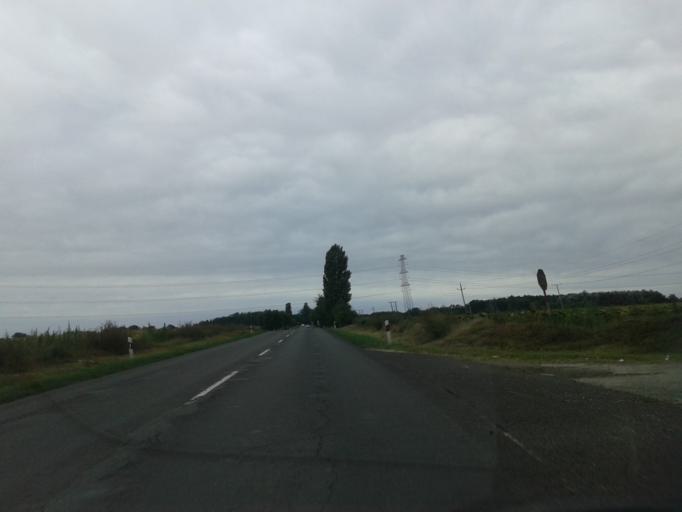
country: HU
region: Pest
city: Dunavarsany
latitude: 47.2467
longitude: 19.0225
